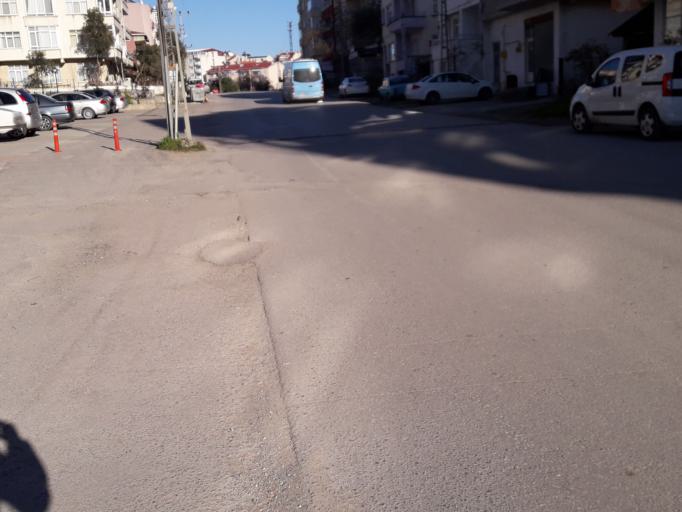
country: TR
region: Sinop
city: Sinop
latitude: 42.0225
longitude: 35.1306
